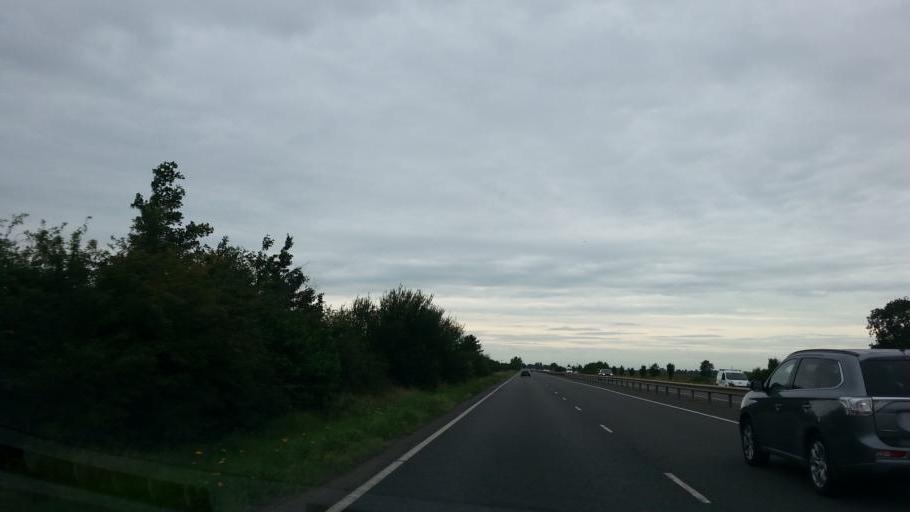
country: GB
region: England
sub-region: Peterborough
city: Thorney
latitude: 52.6230
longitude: -0.0753
